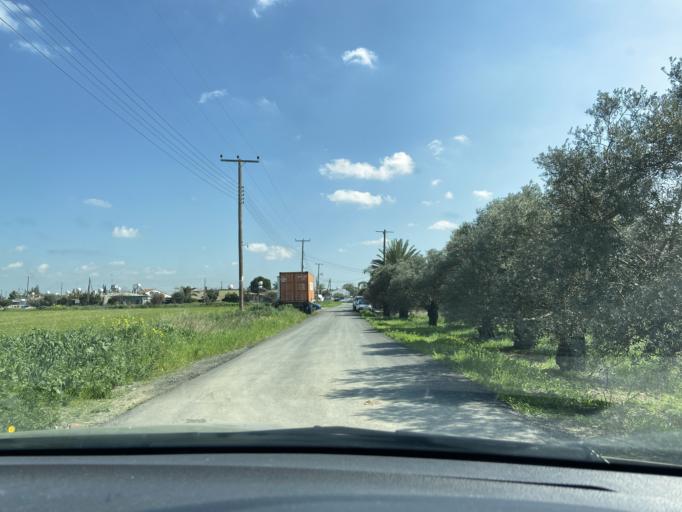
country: CY
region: Lefkosia
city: Alampra
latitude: 35.0200
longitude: 33.3832
